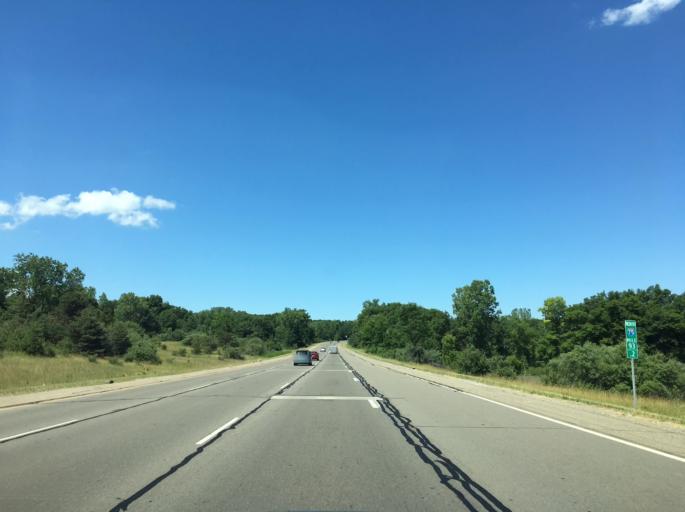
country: US
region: Michigan
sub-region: Oakland County
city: Clarkston
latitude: 42.7399
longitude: -83.4588
